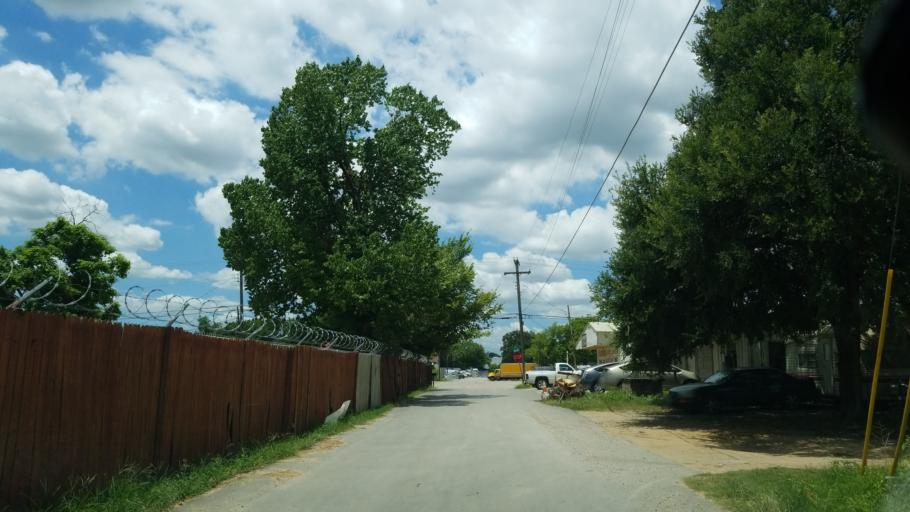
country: US
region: Texas
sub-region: Dallas County
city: Dallas
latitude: 32.7234
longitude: -96.7574
